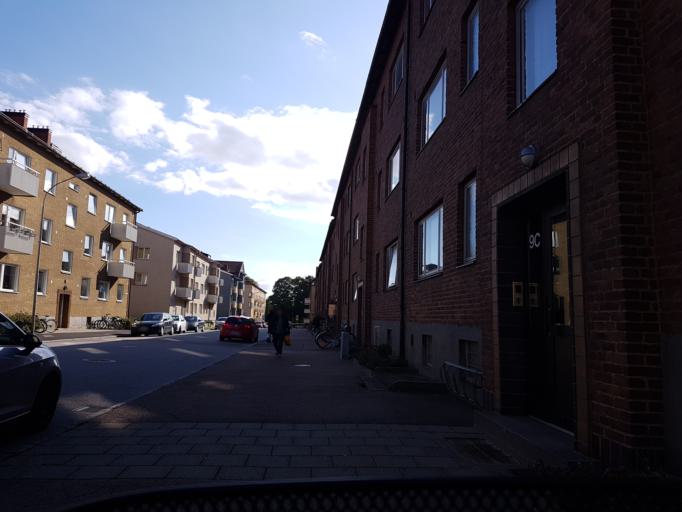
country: SE
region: Skane
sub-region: Landskrona
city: Landskrona
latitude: 55.8782
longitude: 12.8276
